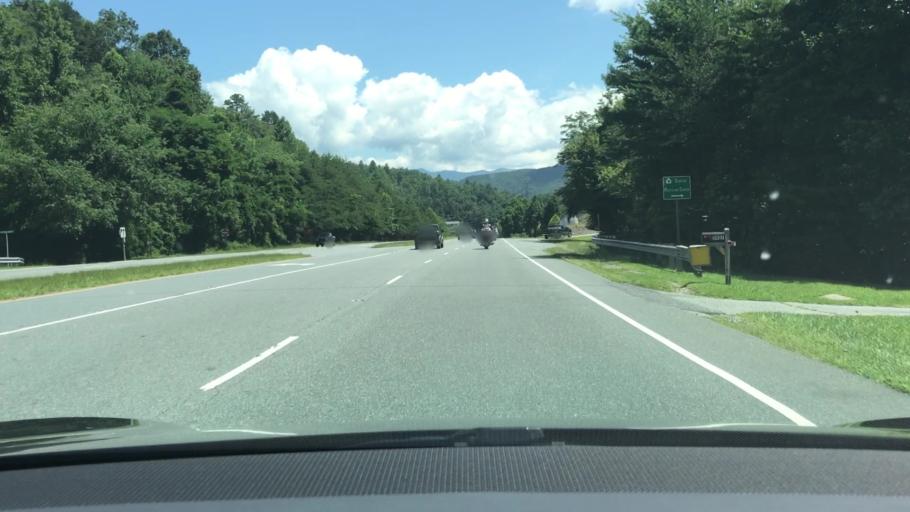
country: US
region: North Carolina
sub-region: Jackson County
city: Sylva
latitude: 35.3295
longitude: -83.2610
